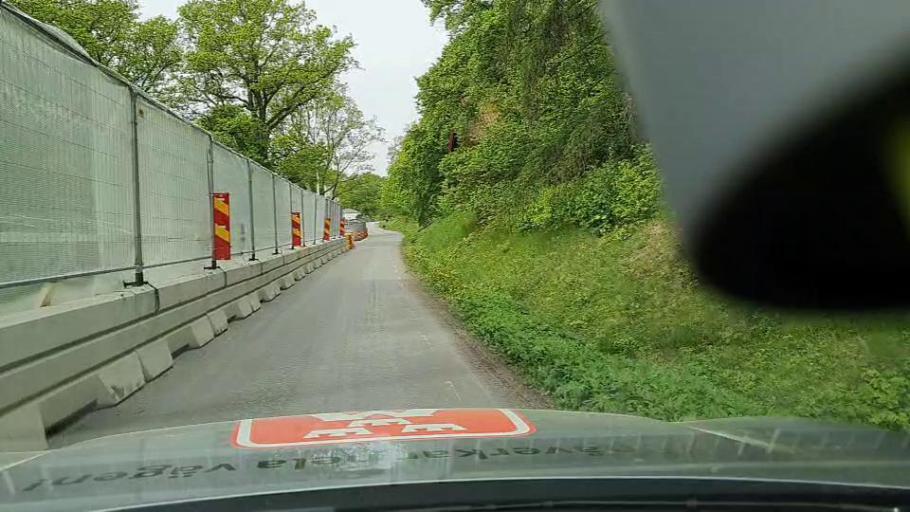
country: SE
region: Soedermanland
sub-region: Flens Kommun
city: Halleforsnas
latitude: 59.0988
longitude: 16.4874
